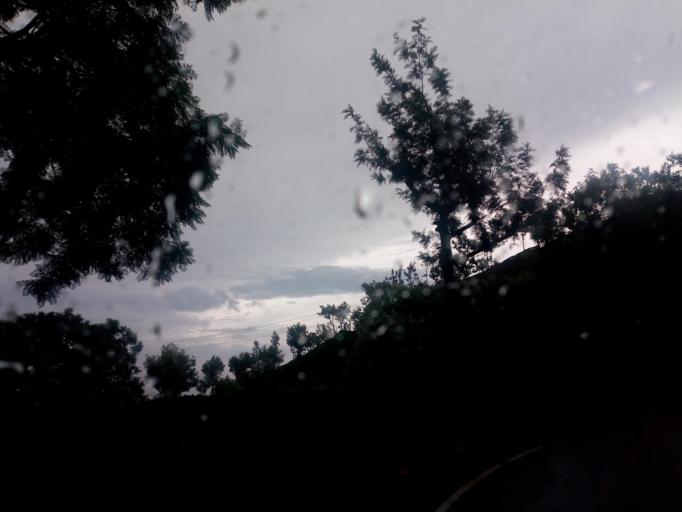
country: IN
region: Tamil Nadu
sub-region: Nilgiri
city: Kotagiri
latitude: 11.3672
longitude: 76.8546
